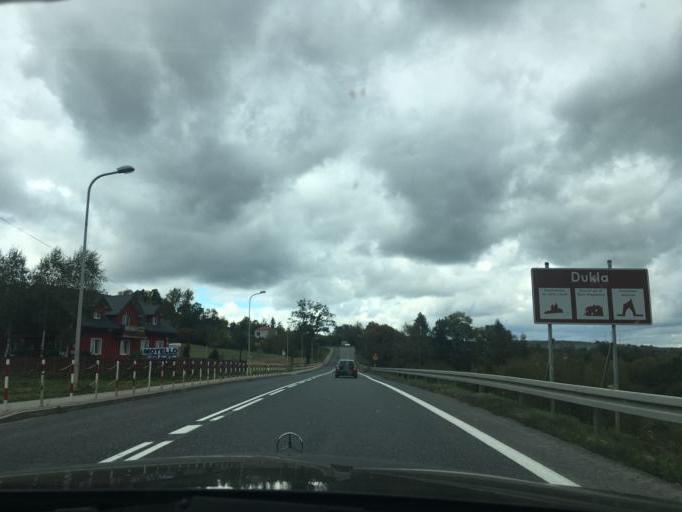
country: PL
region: Subcarpathian Voivodeship
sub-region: Powiat krosnienski
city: Dukla
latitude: 49.5433
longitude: 21.6906
